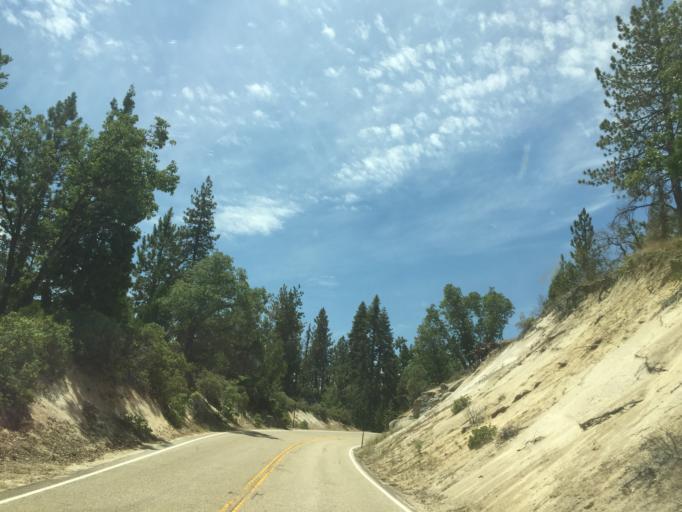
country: US
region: California
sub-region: Fresno County
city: Squaw Valley
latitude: 36.7962
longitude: -118.9535
